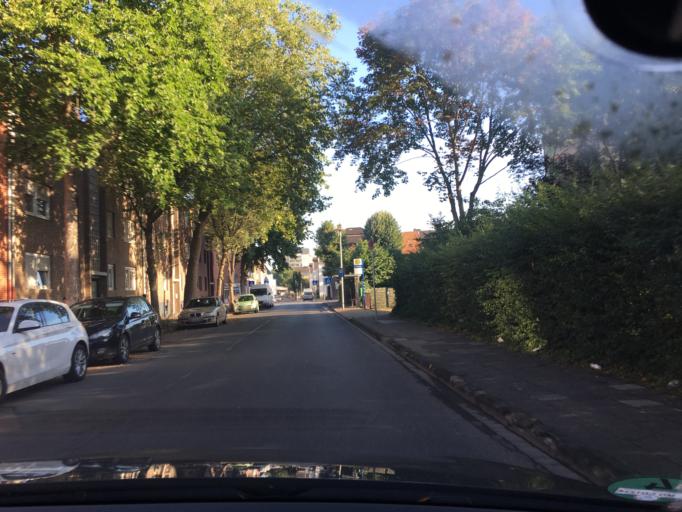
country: DE
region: North Rhine-Westphalia
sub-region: Regierungsbezirk Koln
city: Dueren
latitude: 50.8039
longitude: 6.5007
